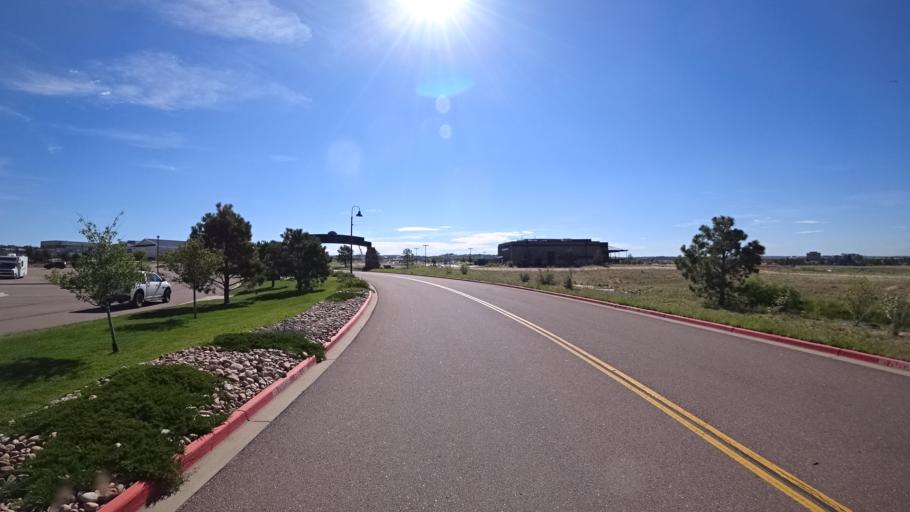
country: US
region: Colorado
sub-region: El Paso County
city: Gleneagle
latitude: 39.0220
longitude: -104.8268
